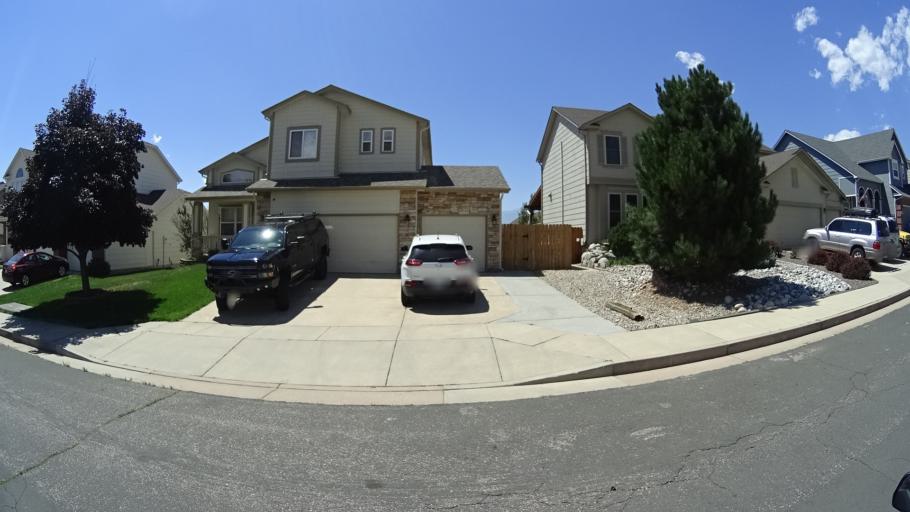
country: US
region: Colorado
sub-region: El Paso County
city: Black Forest
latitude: 38.9526
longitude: -104.7585
